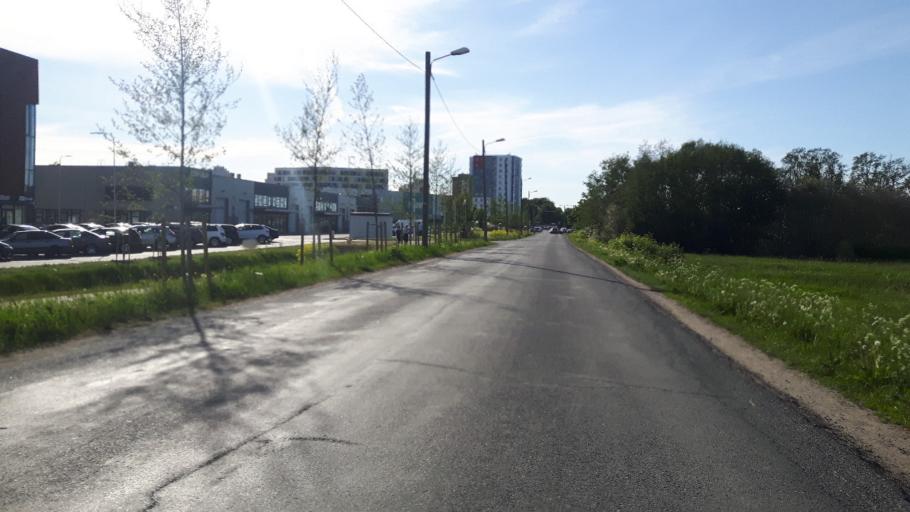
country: EE
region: Harju
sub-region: Tallinna linn
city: Kose
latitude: 59.4513
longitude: 24.8950
